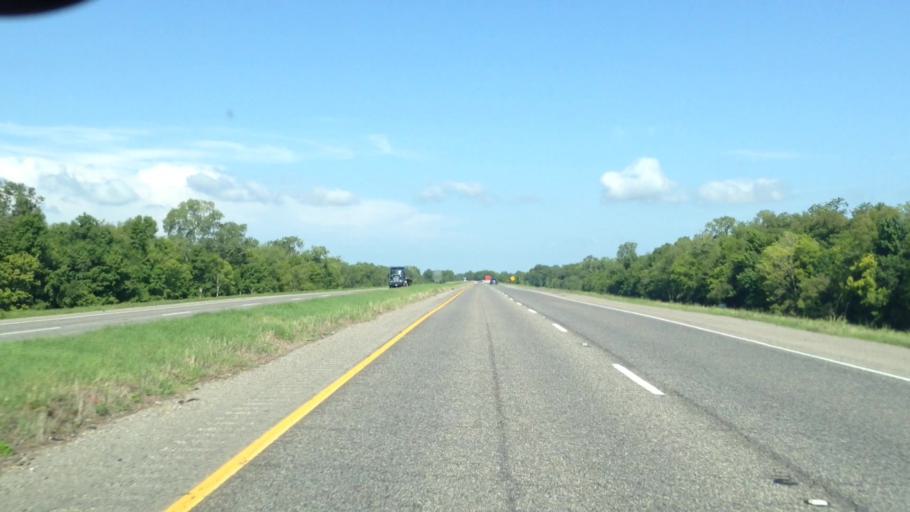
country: US
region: Louisiana
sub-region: Saint Landry Parish
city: Krotz Springs
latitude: 30.5467
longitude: -91.8192
